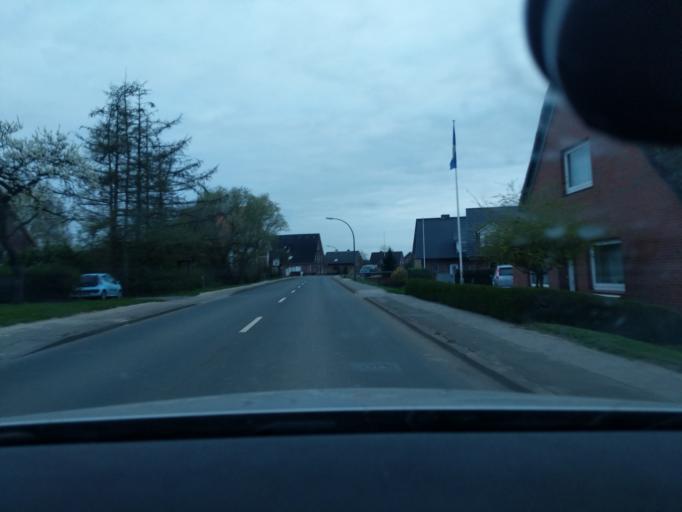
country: DE
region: Lower Saxony
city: Neu Wulmstorf
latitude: 53.5136
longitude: 9.8069
